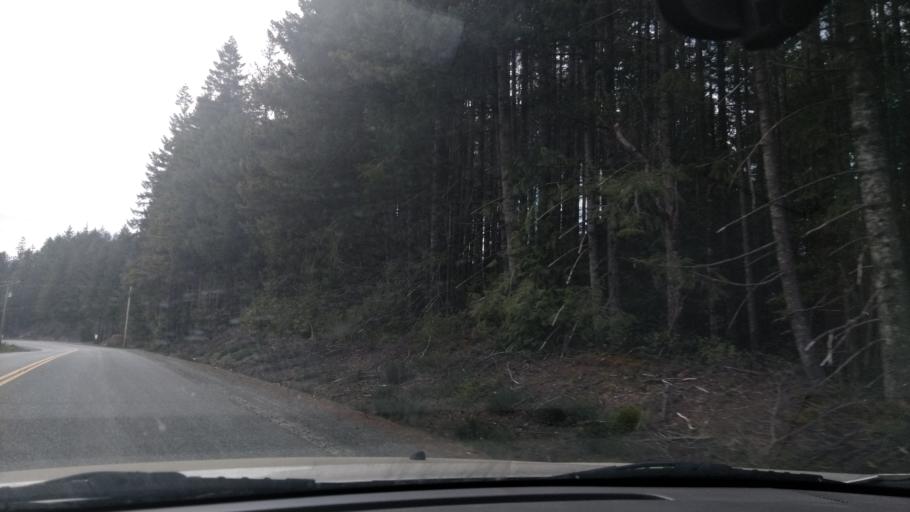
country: CA
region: British Columbia
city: Campbell River
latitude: 50.0040
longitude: -125.3676
